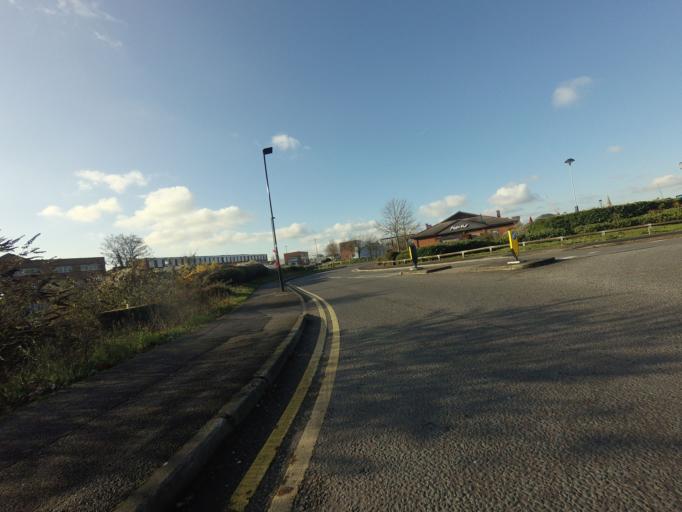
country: GB
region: England
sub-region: Greater London
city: Feltham
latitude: 51.4425
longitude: -0.4045
